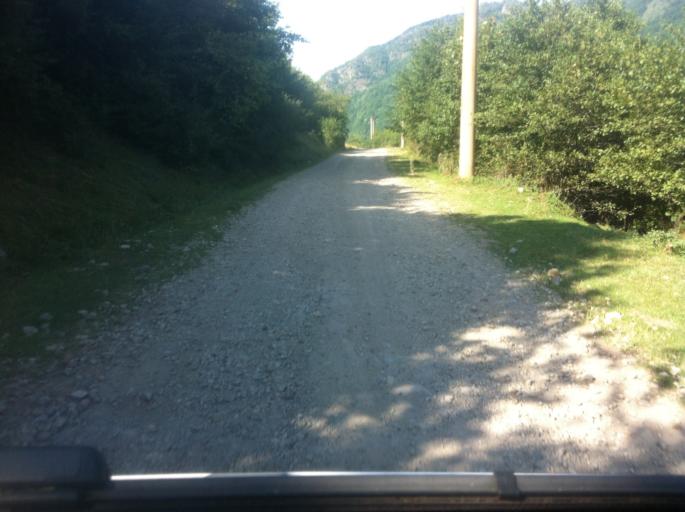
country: RO
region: Hunedoara
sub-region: Comuna Rau de Mori
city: Rau de Mori
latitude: 45.4461
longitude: 22.8943
